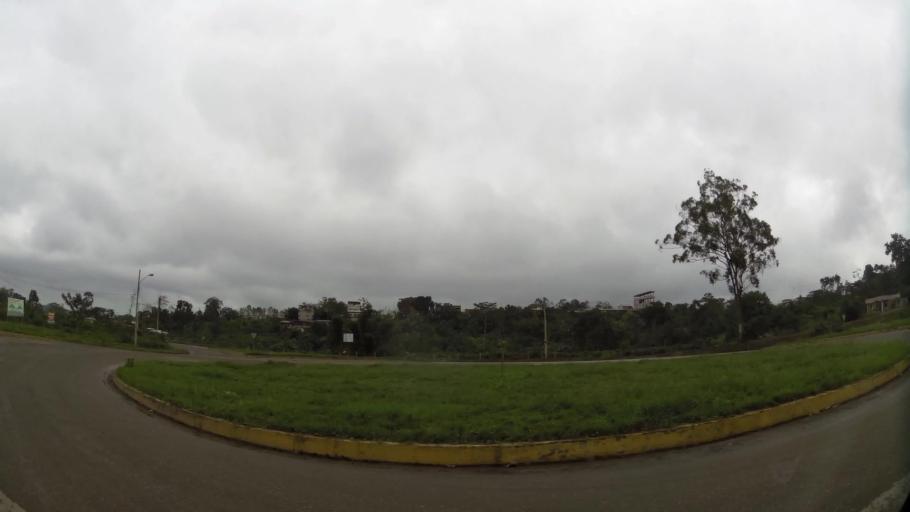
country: EC
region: El Oro
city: Pasaje
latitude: -3.3282
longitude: -79.7716
